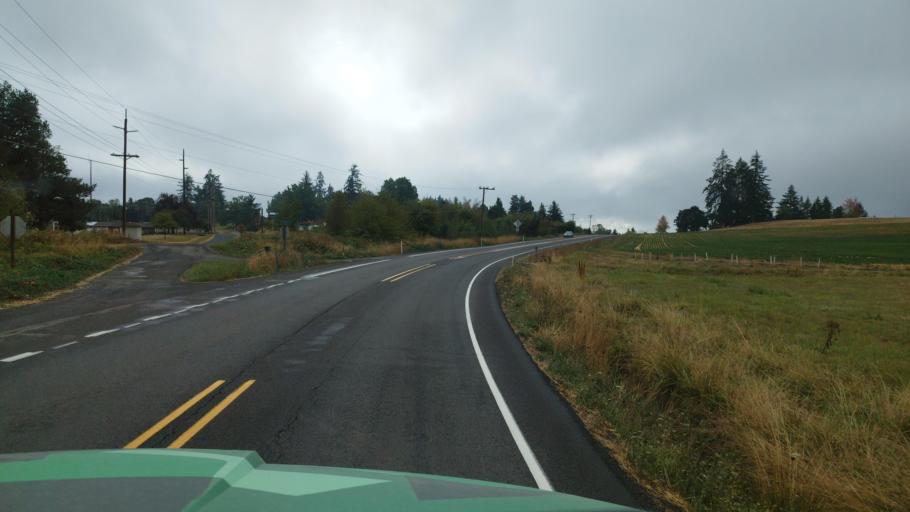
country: US
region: Oregon
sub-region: Yamhill County
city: Yamhill
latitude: 45.3195
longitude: -123.1762
